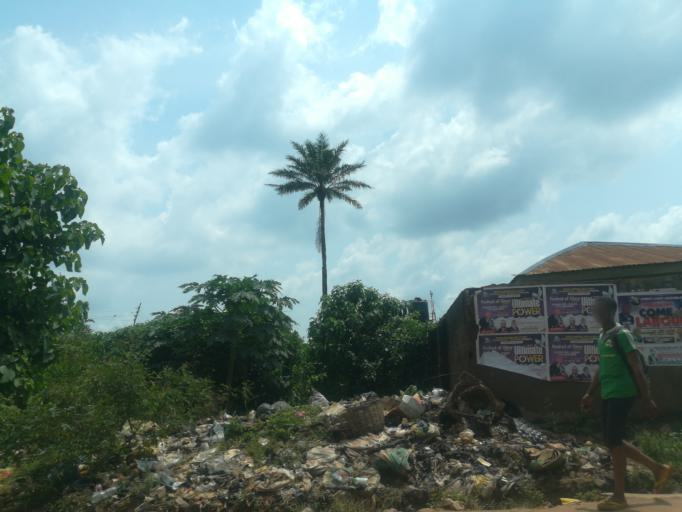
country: NG
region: Oyo
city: Ibadan
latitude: 7.4496
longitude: 3.9539
